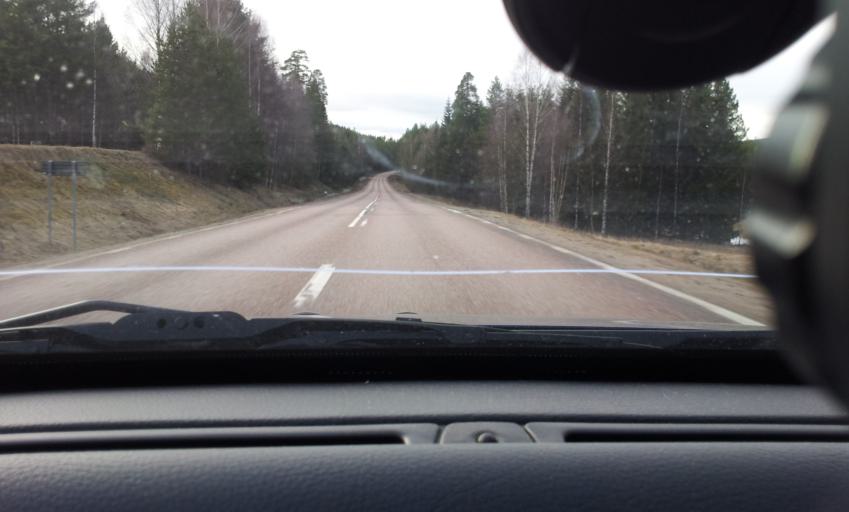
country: SE
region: Gaevleborg
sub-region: Ljusdals Kommun
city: Farila
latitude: 61.8770
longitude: 15.7183
